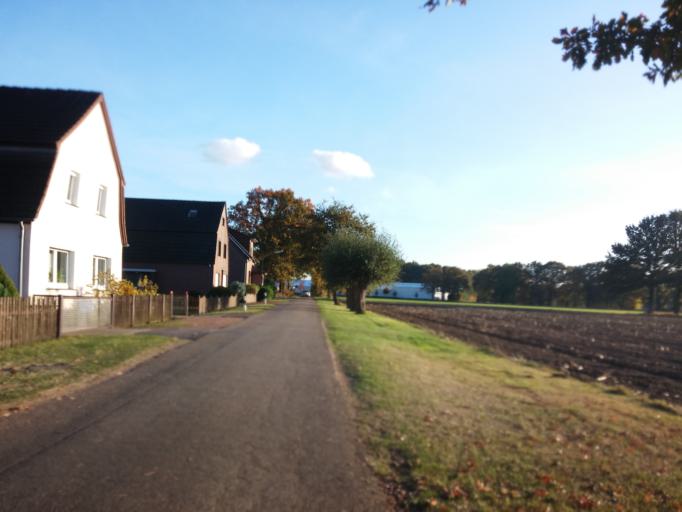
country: DE
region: North Rhine-Westphalia
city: Dorsten
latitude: 51.6393
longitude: 6.9832
